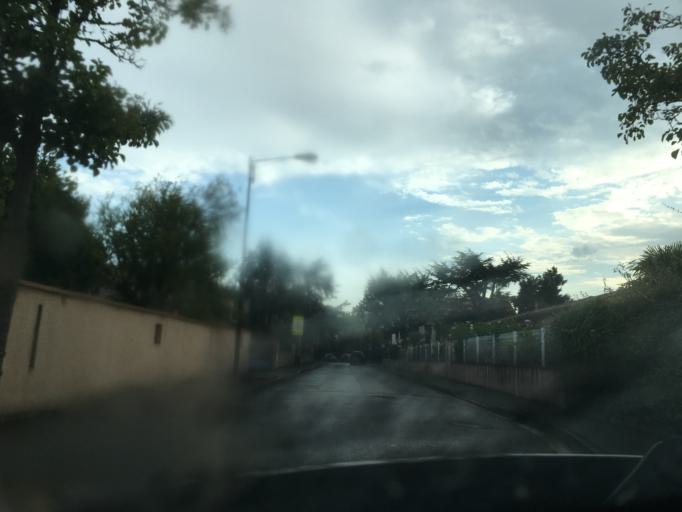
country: FR
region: Midi-Pyrenees
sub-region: Departement de la Haute-Garonne
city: Cugnaux
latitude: 43.5583
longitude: 1.3766
